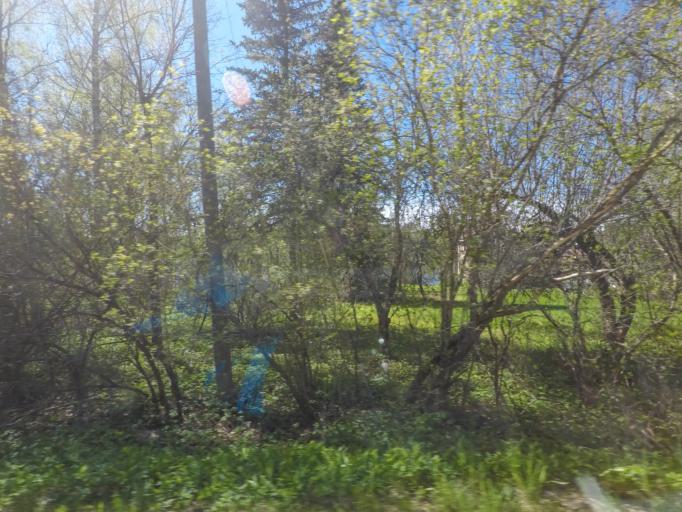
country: FI
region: Uusimaa
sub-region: Helsinki
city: Sammatti
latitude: 60.3431
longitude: 23.8021
